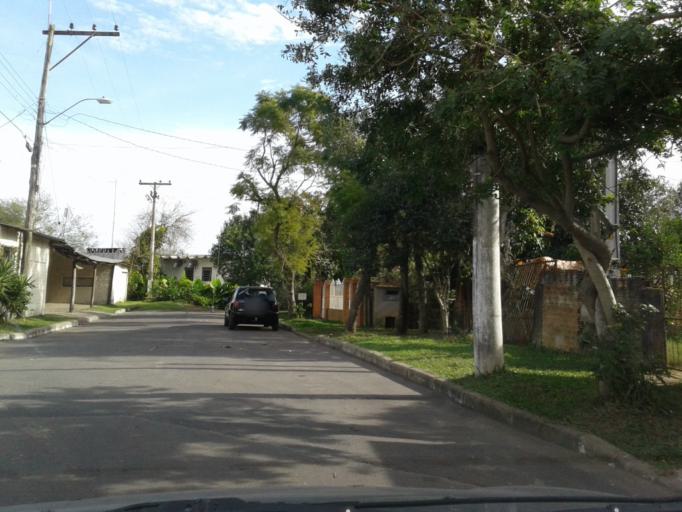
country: BR
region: Rio Grande do Sul
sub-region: Porto Alegre
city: Porto Alegre
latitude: -30.0155
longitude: -51.2607
